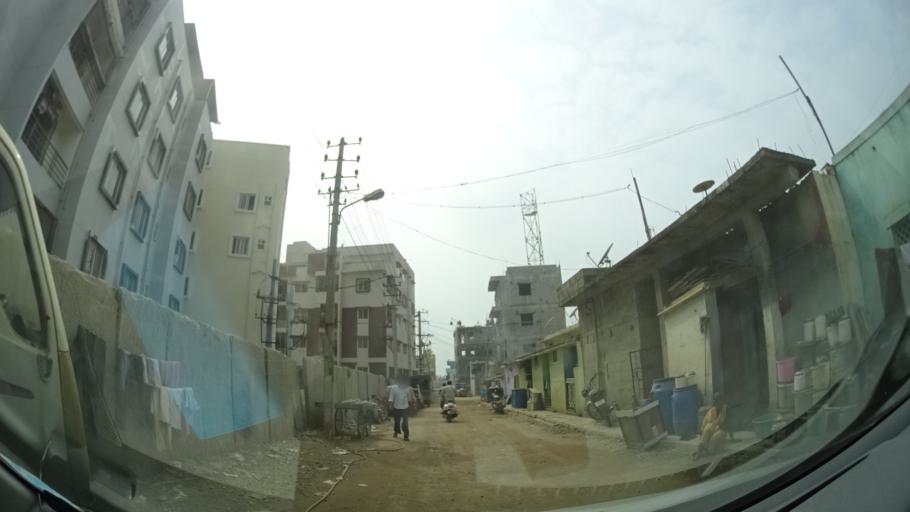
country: IN
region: Karnataka
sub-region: Bangalore Rural
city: Hoskote
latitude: 12.9762
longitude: 77.7570
